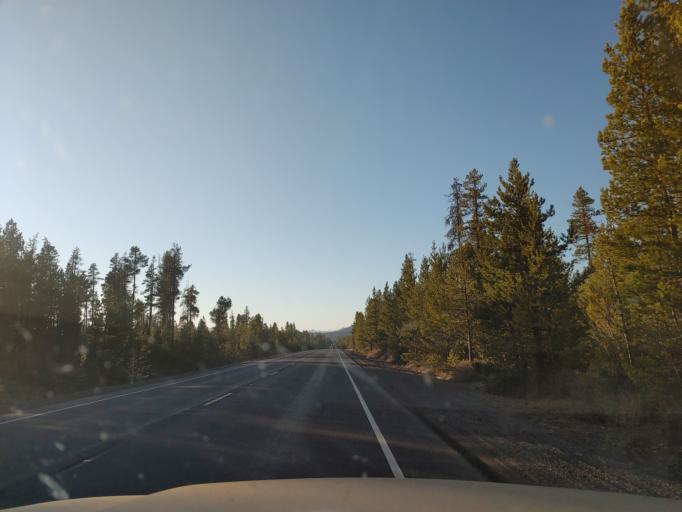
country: US
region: Oregon
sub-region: Deschutes County
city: La Pine
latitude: 43.3997
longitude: -121.8203
